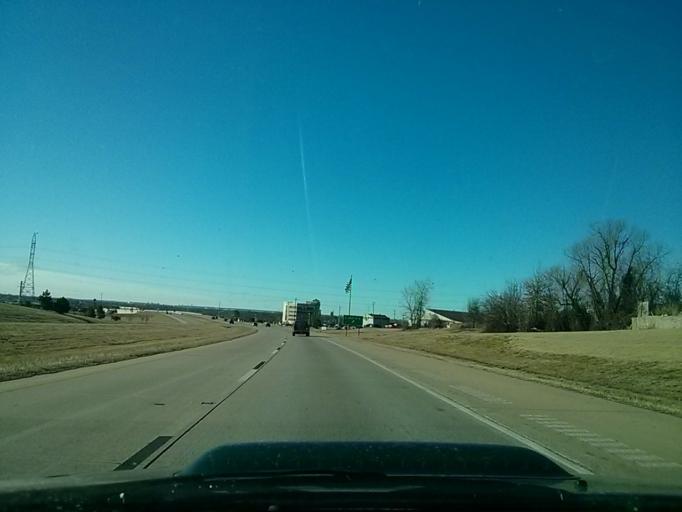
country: US
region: Oklahoma
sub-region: Tulsa County
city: Owasso
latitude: 36.2844
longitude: -95.8459
